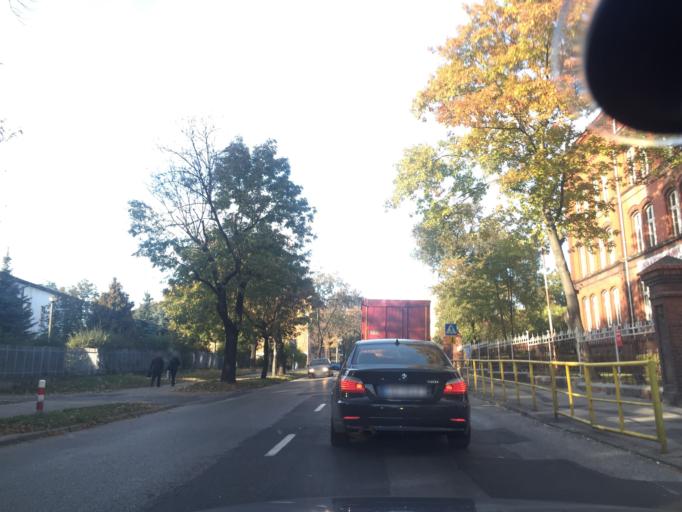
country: PL
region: Kujawsko-Pomorskie
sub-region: Powiat inowroclawski
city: Inowroclaw
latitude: 52.7984
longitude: 18.2644
